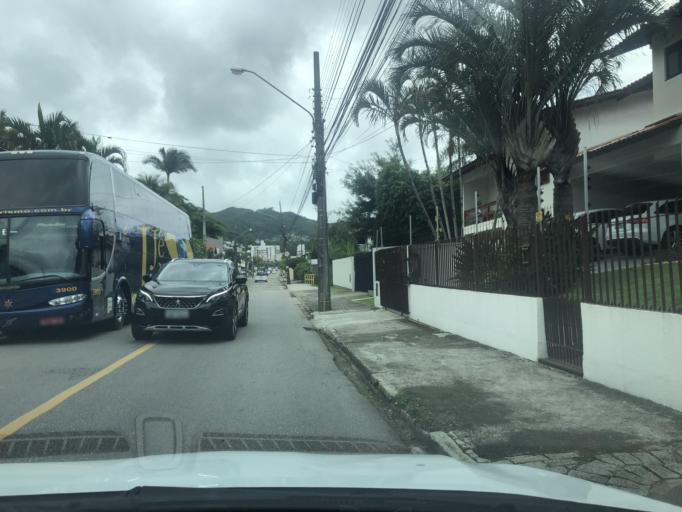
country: BR
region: Santa Catarina
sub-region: Florianopolis
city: Santa Monica
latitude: -27.5942
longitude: -48.5122
